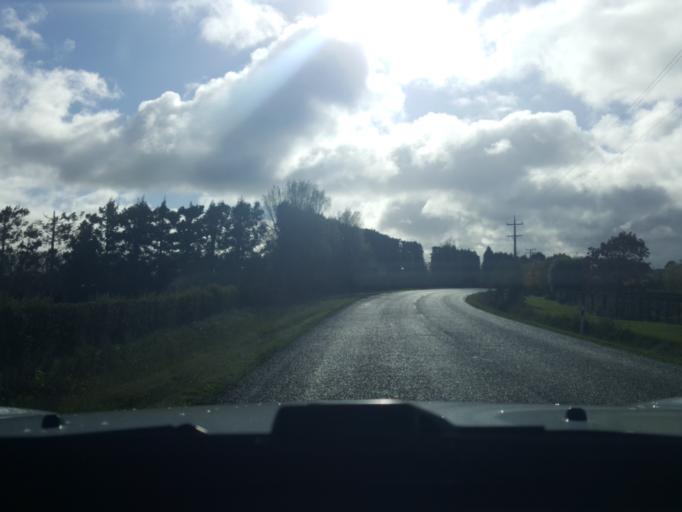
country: NZ
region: Auckland
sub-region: Auckland
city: Pukekohe East
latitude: -37.3052
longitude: 175.0132
